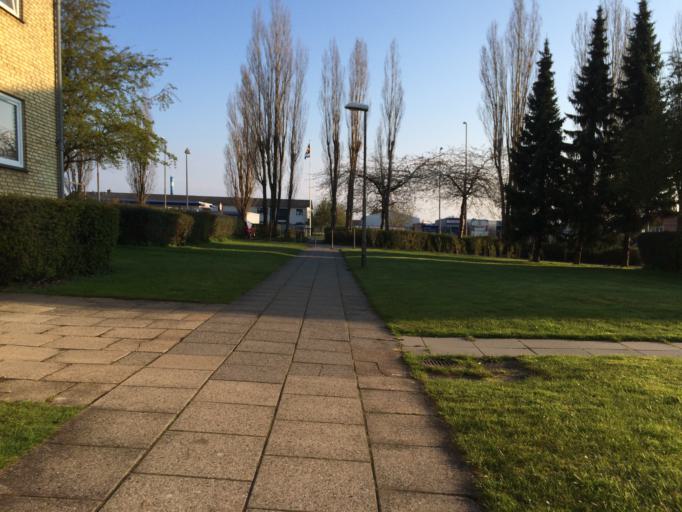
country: DK
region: Capital Region
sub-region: Hoje-Taastrup Kommune
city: Taastrup
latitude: 55.6459
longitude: 12.2888
